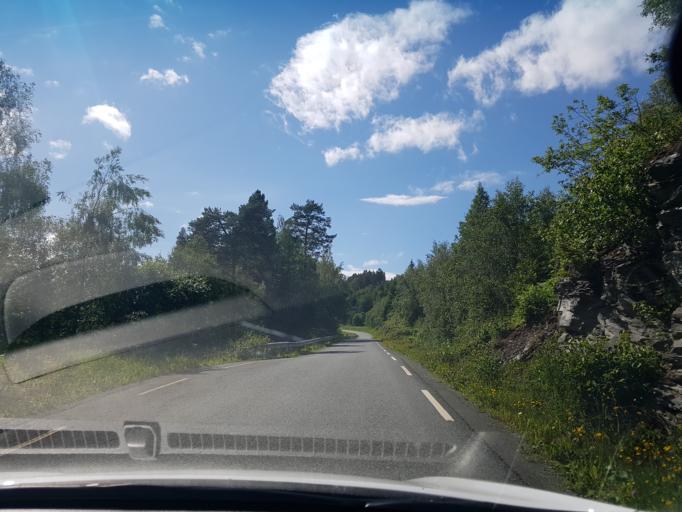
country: NO
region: Nord-Trondelag
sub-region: Frosta
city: Frosta
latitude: 63.6060
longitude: 10.8404
